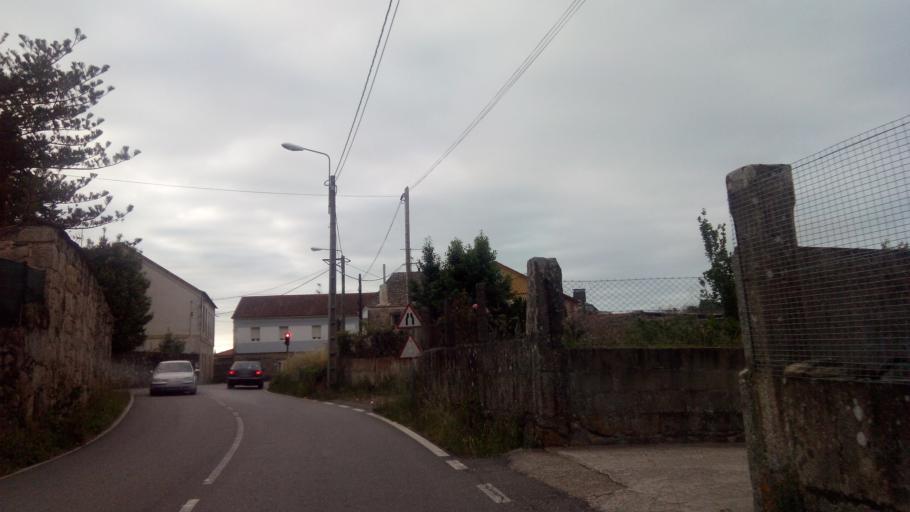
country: ES
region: Galicia
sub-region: Provincia de Pontevedra
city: Nigran
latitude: 42.1241
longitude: -8.8036
